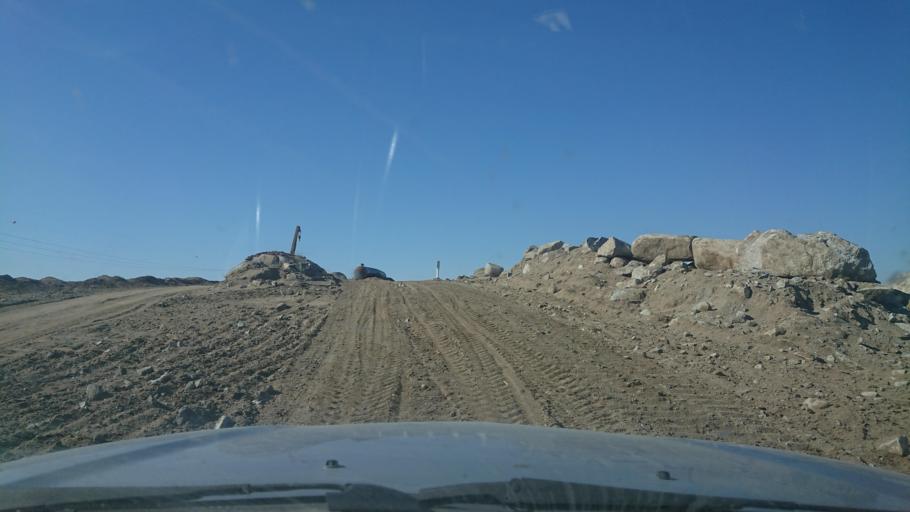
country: TR
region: Aksaray
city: Agacoren
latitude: 38.8439
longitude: 33.9439
